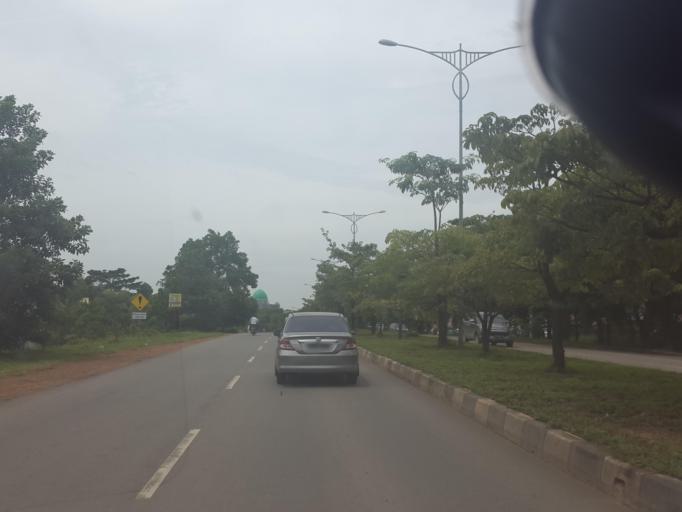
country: SG
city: Singapore
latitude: 1.1072
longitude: 104.0647
